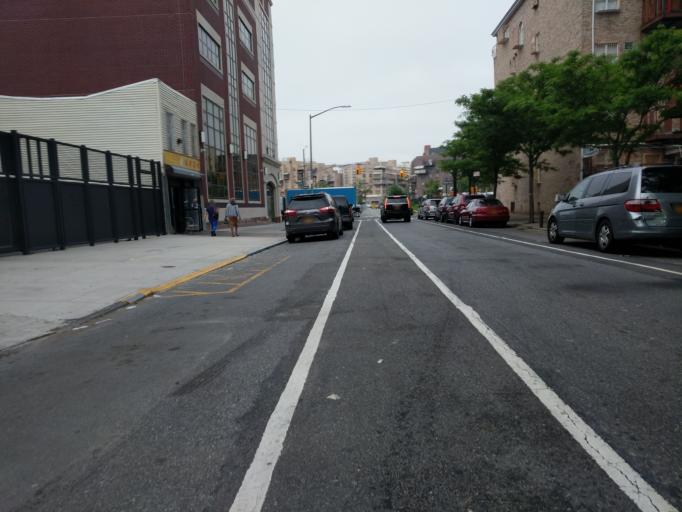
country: US
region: New York
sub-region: Queens County
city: Long Island City
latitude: 40.7019
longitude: -73.9481
